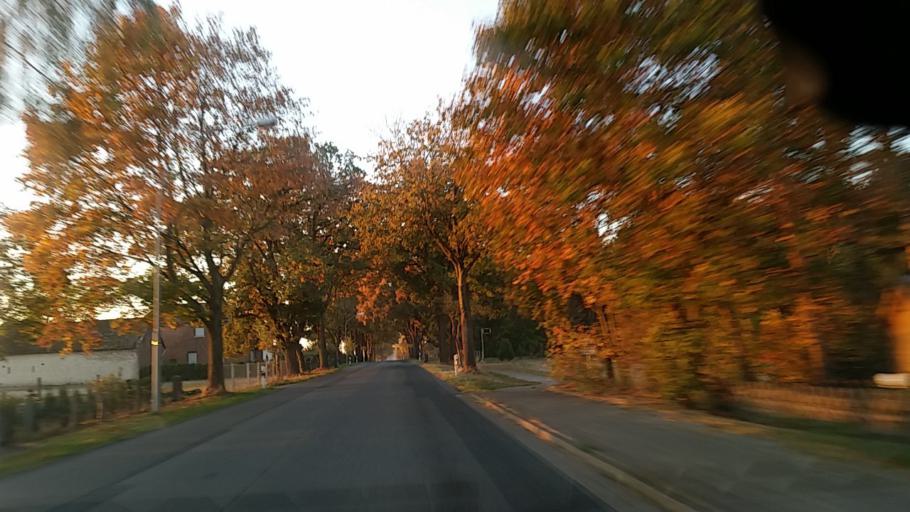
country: DE
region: Lower Saxony
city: Bodenteich
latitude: 52.8557
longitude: 10.6818
